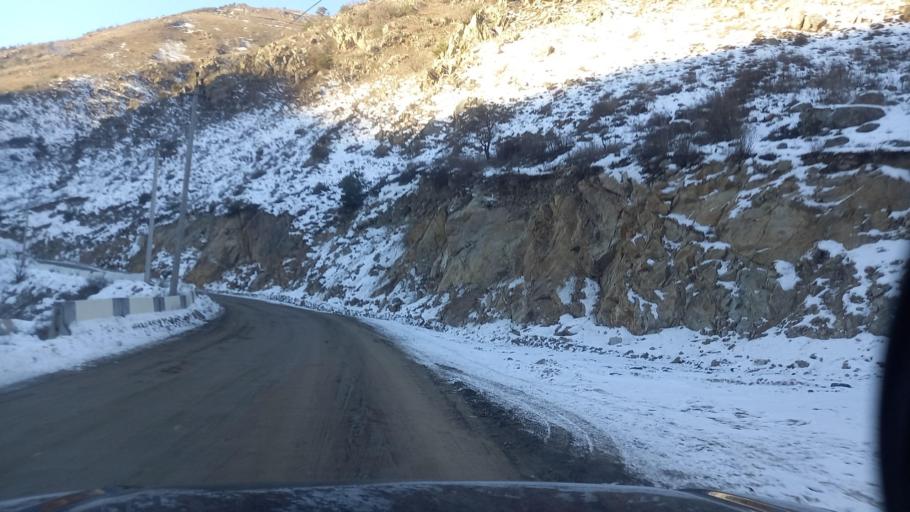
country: RU
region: North Ossetia
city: Chikola
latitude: 42.9801
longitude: 43.7709
